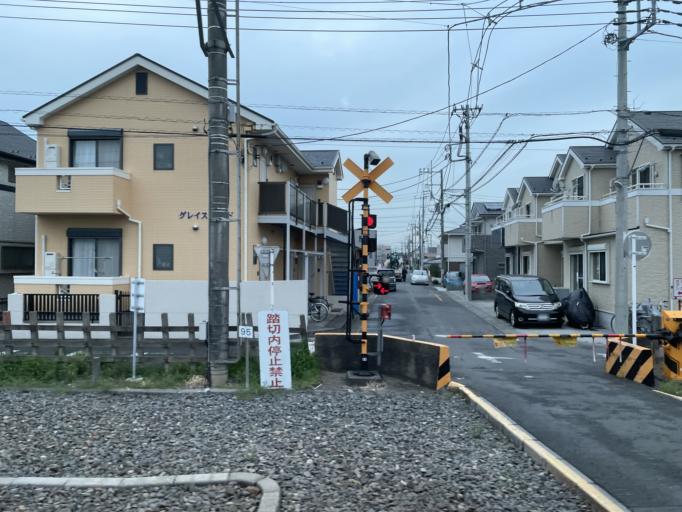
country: JP
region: Saitama
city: Koshigaya
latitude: 35.9263
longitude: 139.7773
